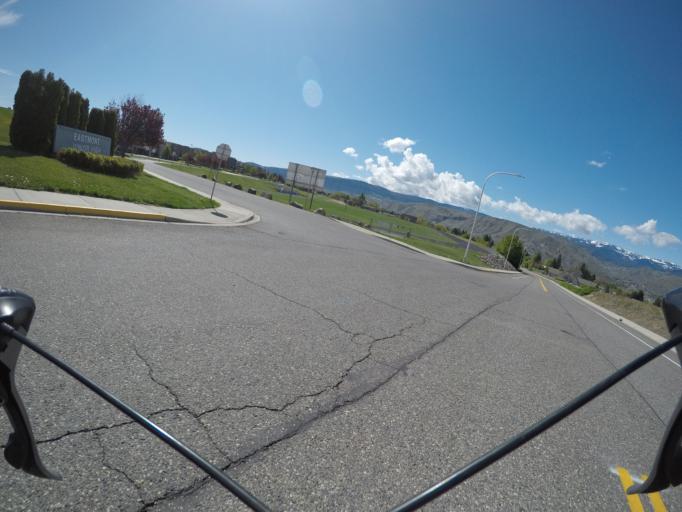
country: US
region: Washington
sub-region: Douglas County
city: East Wenatchee Bench
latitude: 47.4197
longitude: -120.2758
